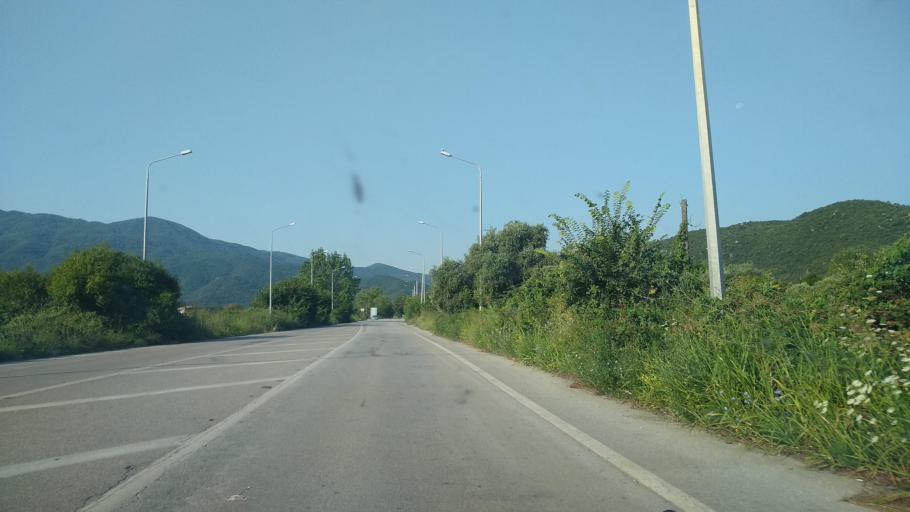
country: GR
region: Central Macedonia
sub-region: Nomos Thessalonikis
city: Nea Vrasna
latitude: 40.6901
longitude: 23.6818
